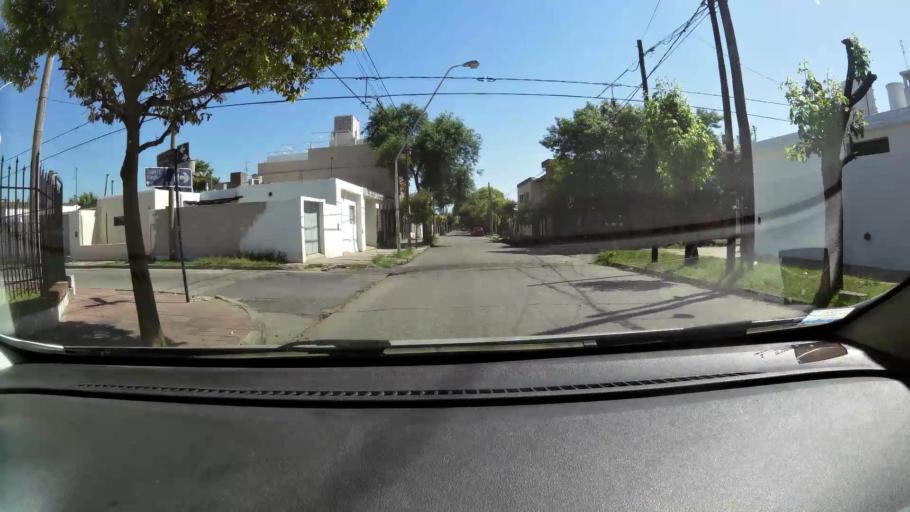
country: AR
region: Cordoba
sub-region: Departamento de Capital
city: Cordoba
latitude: -31.4183
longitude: -64.2162
